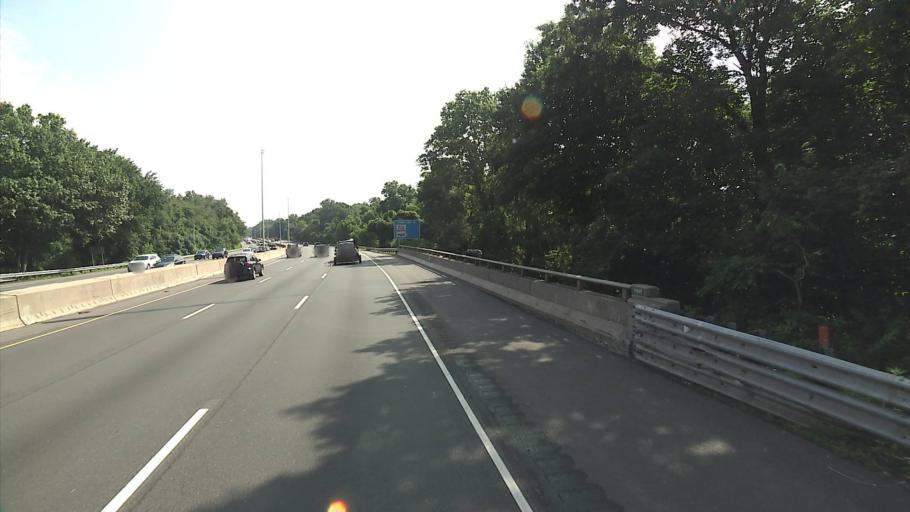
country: US
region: Connecticut
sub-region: Fairfield County
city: Darien
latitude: 41.0910
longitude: -73.4497
